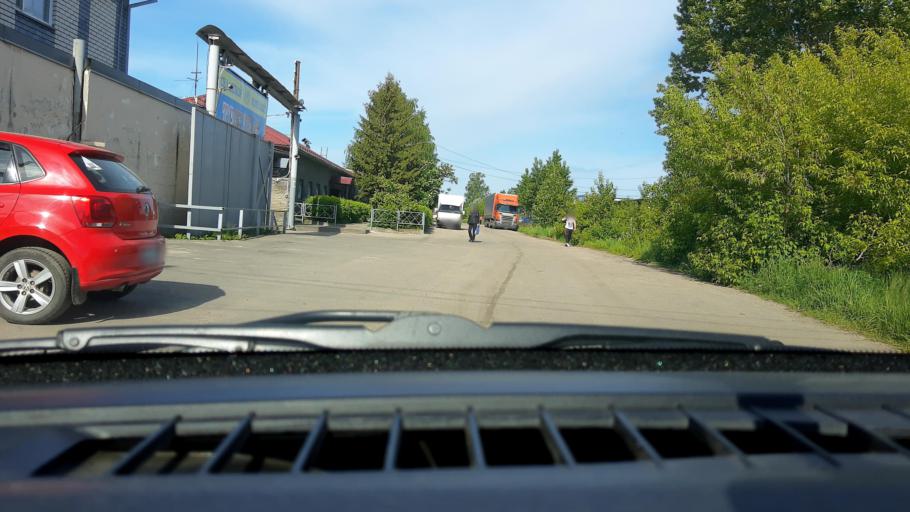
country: RU
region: Nizjnij Novgorod
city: Gorbatovka
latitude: 56.3386
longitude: 43.8103
